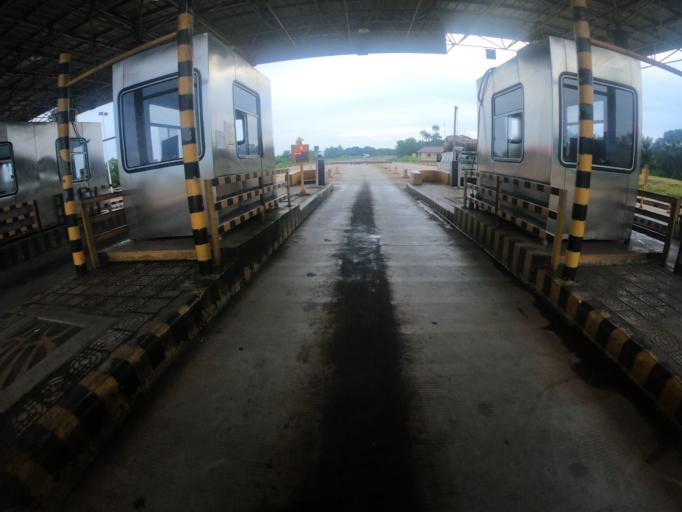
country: SL
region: Northern Province
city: Port Loko
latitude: 8.4878
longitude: -12.7839
